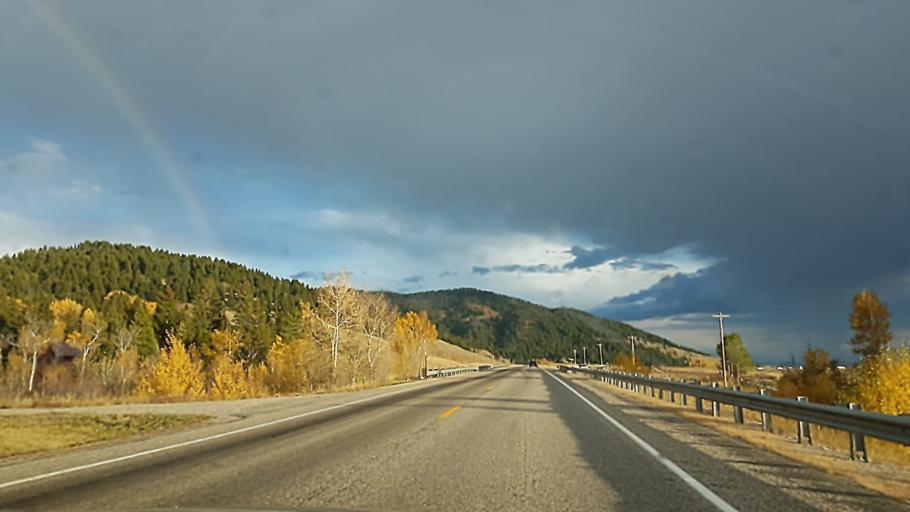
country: US
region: Montana
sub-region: Gallatin County
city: West Yellowstone
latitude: 44.6474
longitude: -111.3431
